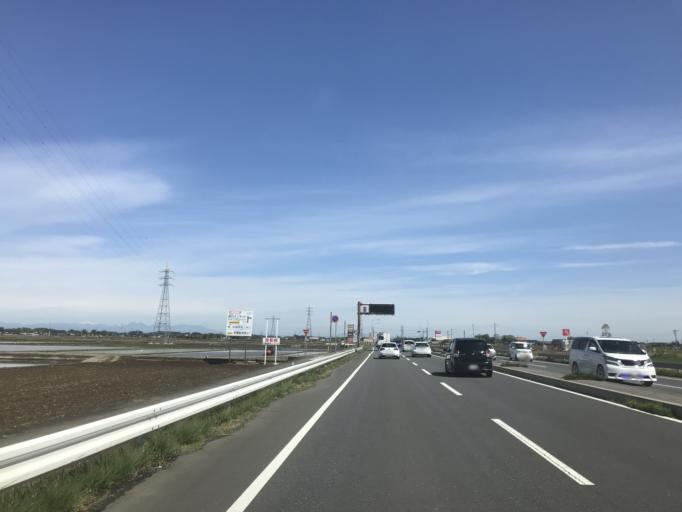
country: JP
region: Ibaraki
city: Ishige
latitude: 36.1770
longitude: 139.9909
